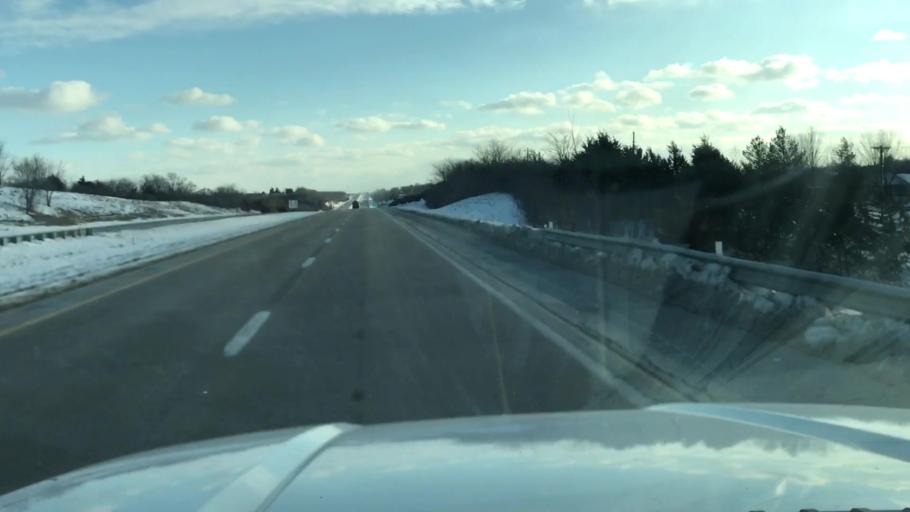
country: US
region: Missouri
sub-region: Andrew County
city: Savannah
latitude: 39.9474
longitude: -94.8603
